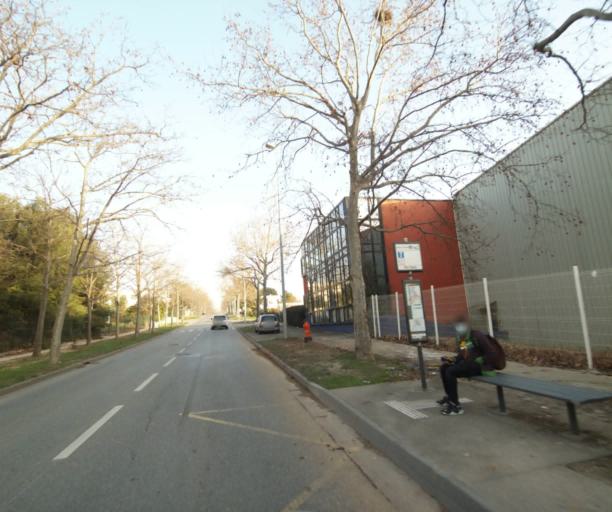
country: FR
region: Provence-Alpes-Cote d'Azur
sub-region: Departement des Bouches-du-Rhone
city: Saint-Victoret
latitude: 43.4227
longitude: 5.2612
